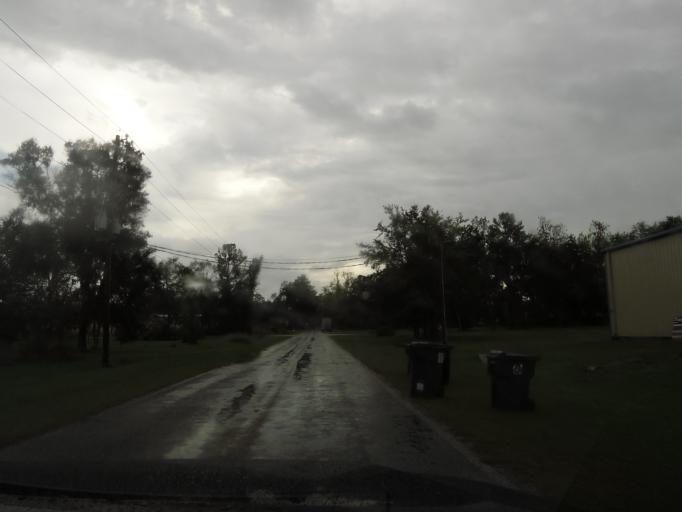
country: US
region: Florida
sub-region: Nassau County
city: Hilliard
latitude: 30.5244
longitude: -82.0367
